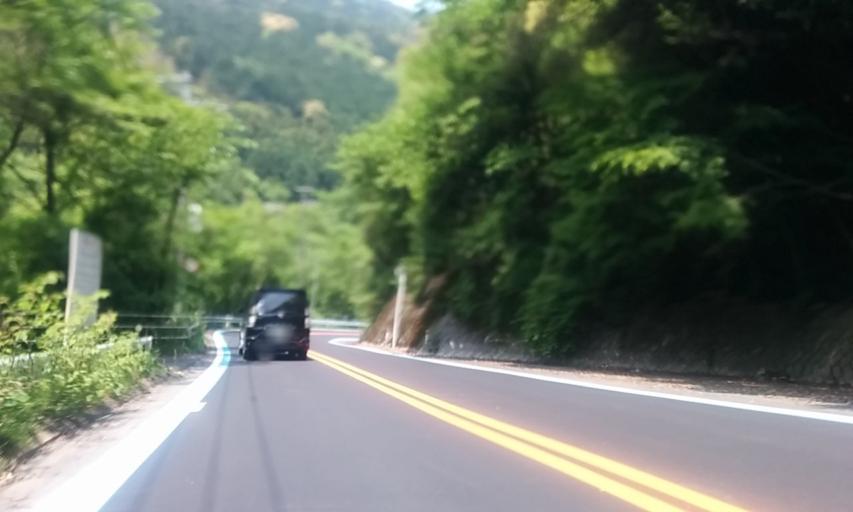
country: JP
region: Ehime
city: Niihama
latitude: 33.9074
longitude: 133.3079
